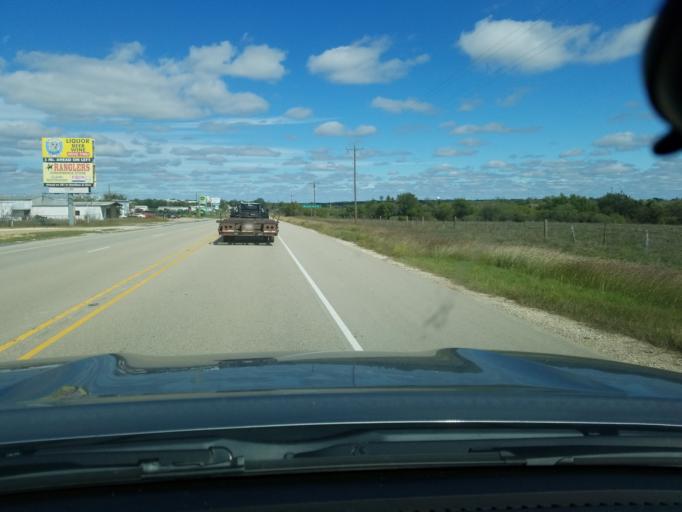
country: US
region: Texas
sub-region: Hamilton County
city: Hamilton
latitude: 31.6784
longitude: -98.1342
